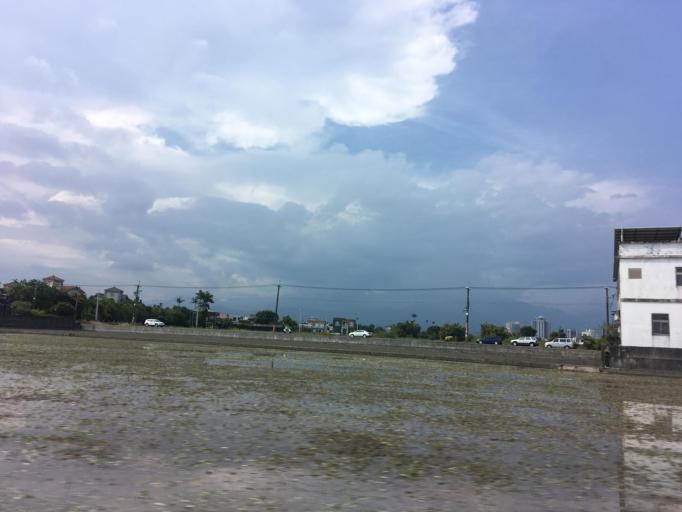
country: TW
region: Taiwan
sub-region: Yilan
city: Yilan
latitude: 24.6926
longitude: 121.7833
